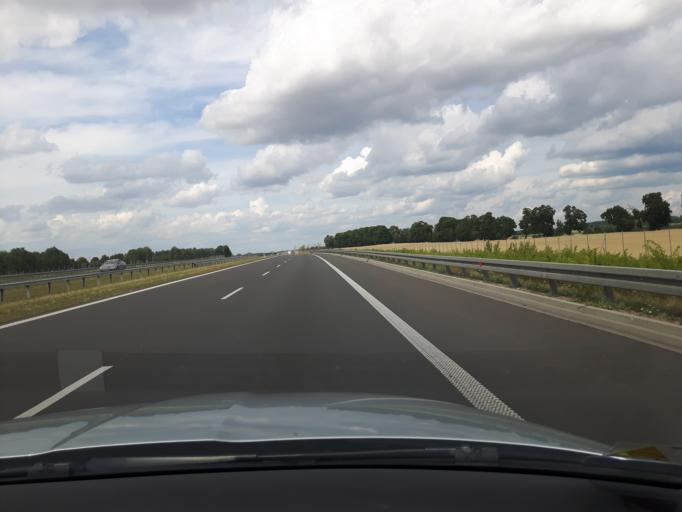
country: PL
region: Warmian-Masurian Voivodeship
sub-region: Powiat nidzicki
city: Nidzica
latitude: 53.2873
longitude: 20.4392
